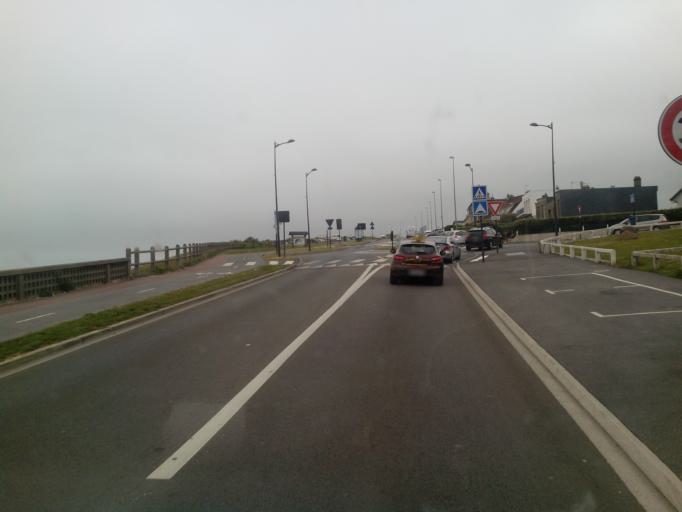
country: FR
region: Nord-Pas-de-Calais
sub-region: Departement du Pas-de-Calais
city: Saint-Martin-Boulogne
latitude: 50.7401
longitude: 1.5950
